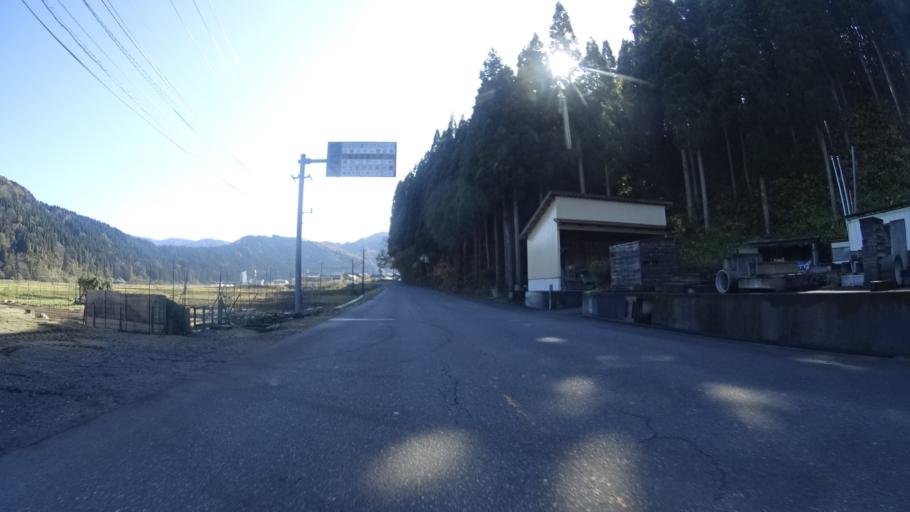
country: JP
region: Ishikawa
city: Tsurugi-asahimachi
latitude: 36.3631
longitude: 136.5939
